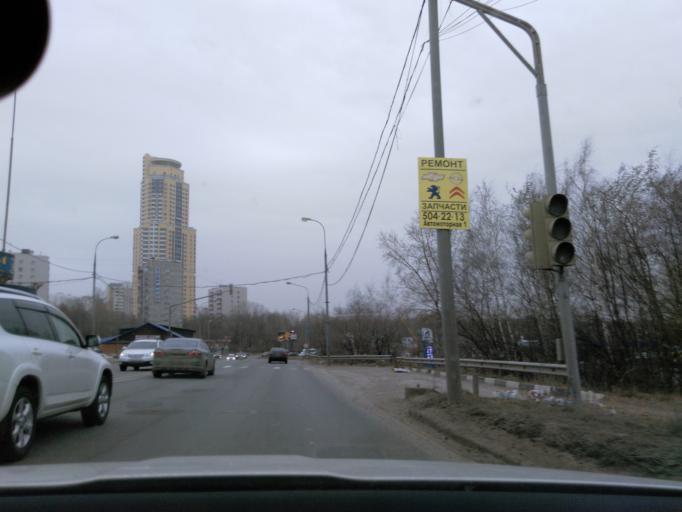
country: RU
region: Moskovskaya
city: Levoberezhnaya
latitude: 55.8809
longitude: 37.4825
